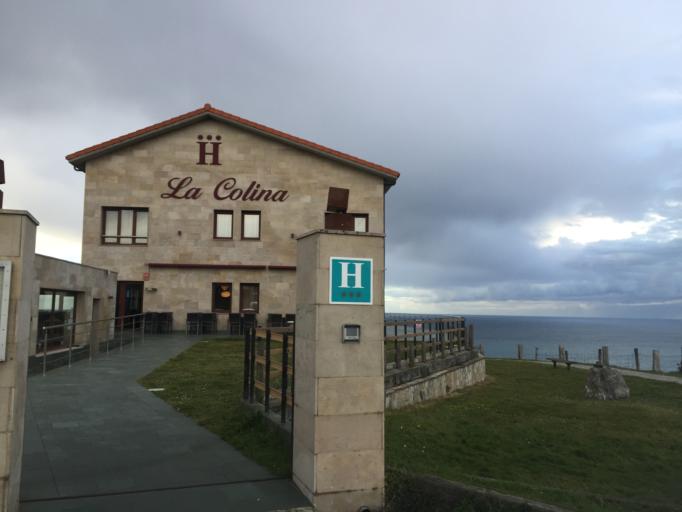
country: ES
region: Asturias
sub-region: Province of Asturias
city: Gijon
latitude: 43.5519
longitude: -5.6143
